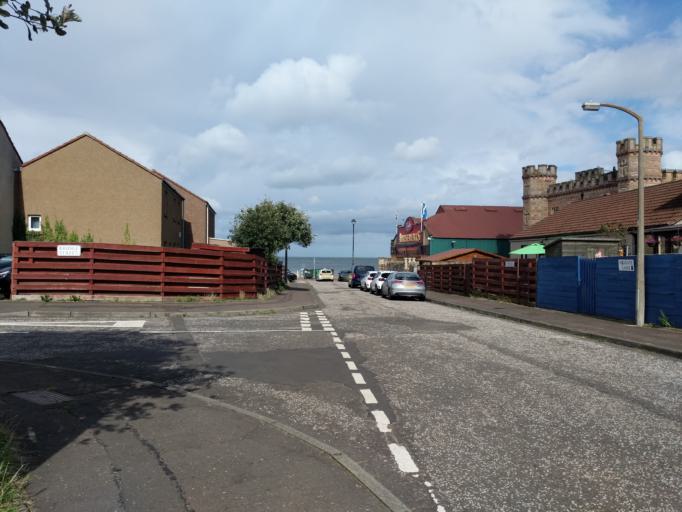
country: GB
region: Scotland
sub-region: West Lothian
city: Seafield
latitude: 55.9555
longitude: -3.1138
